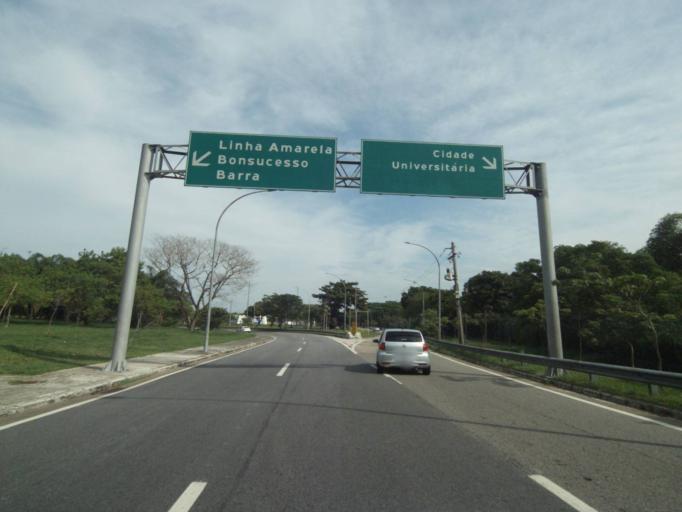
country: BR
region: Rio de Janeiro
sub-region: Rio De Janeiro
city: Rio de Janeiro
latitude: -22.8603
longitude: -43.2325
